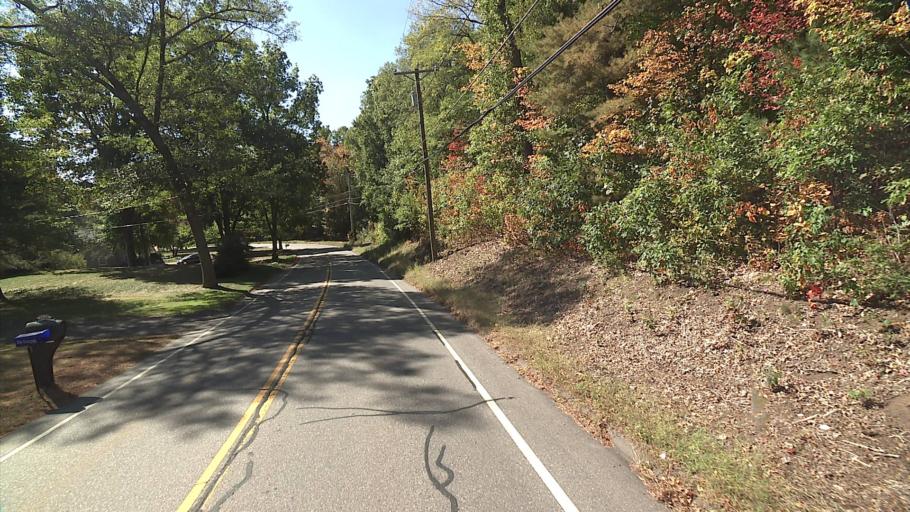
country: US
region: Connecticut
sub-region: Hartford County
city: Manchester
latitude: 41.7199
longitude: -72.5265
